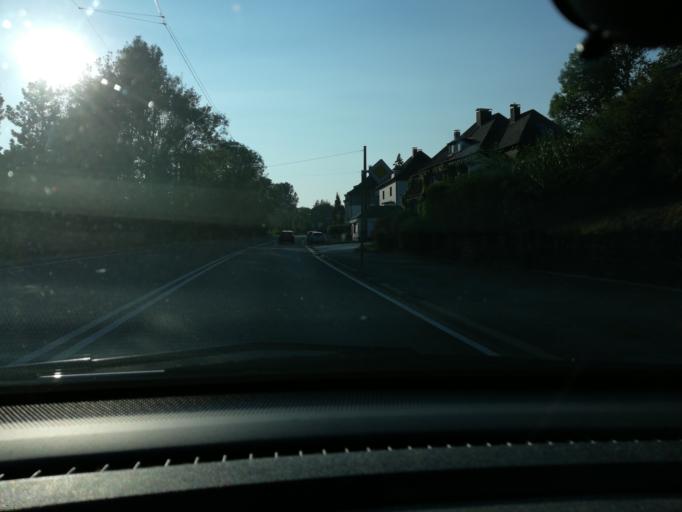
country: DE
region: North Rhine-Westphalia
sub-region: Regierungsbezirk Arnsberg
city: Schwelm
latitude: 51.2970
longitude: 7.3202
